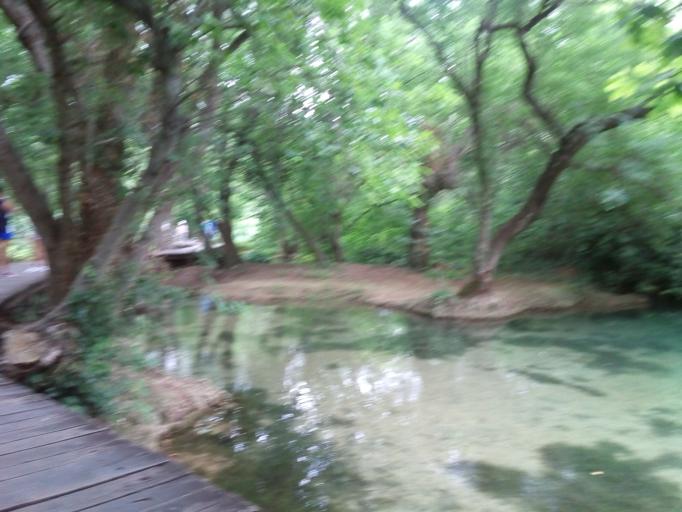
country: HR
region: Sibensko-Kniniska
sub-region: Grad Sibenik
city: Sibenik
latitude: 43.8019
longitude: 15.9654
